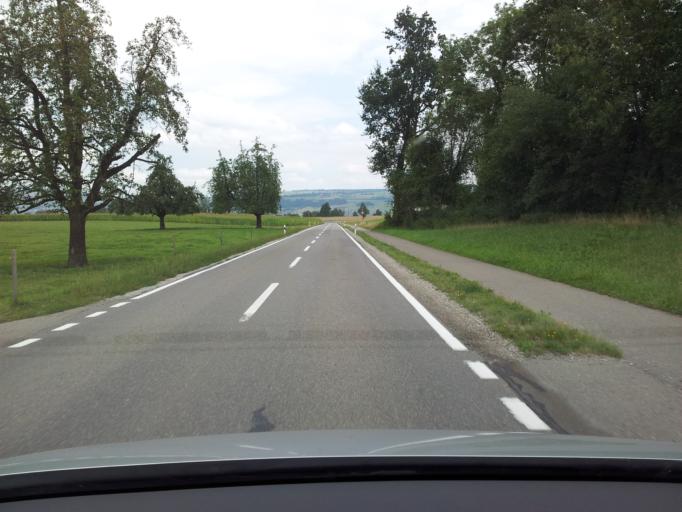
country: CH
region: Lucerne
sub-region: Sursee District
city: Nottwil
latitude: 47.1300
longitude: 8.1167
